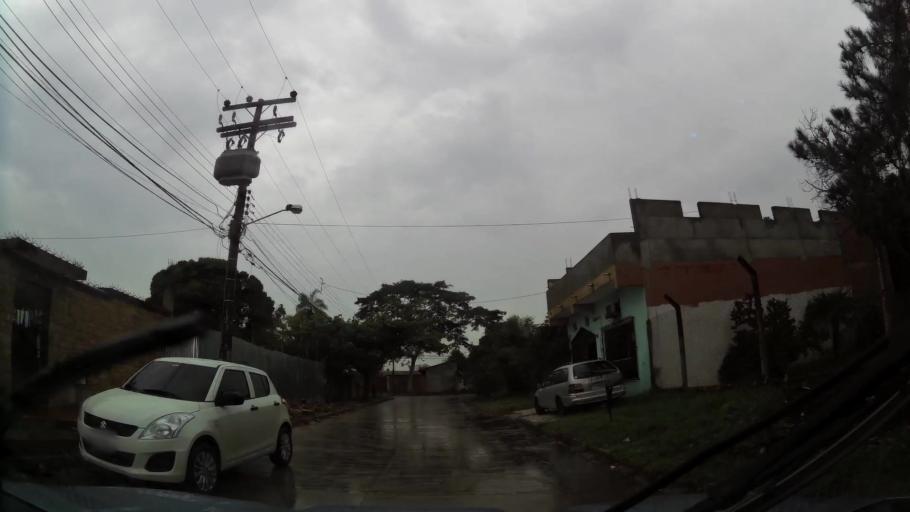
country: BO
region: Santa Cruz
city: Santa Cruz de la Sierra
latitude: -17.7983
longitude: -63.2234
